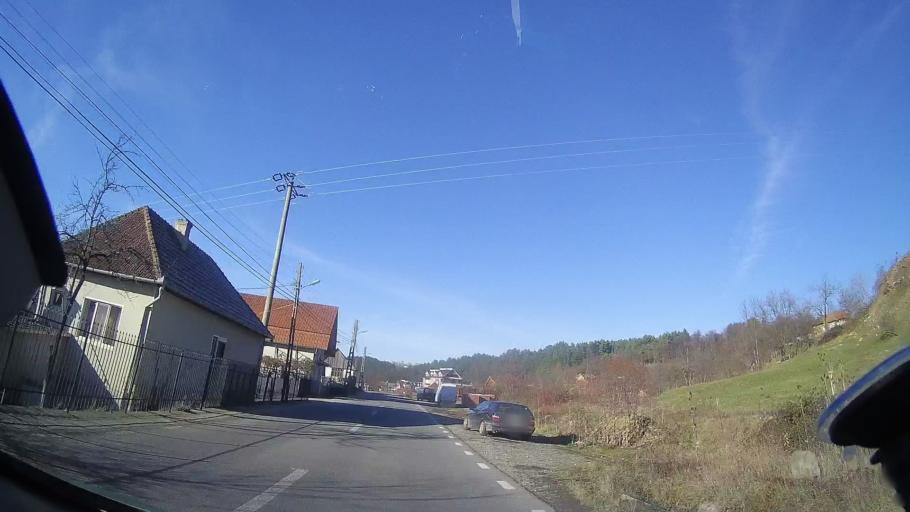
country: RO
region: Bihor
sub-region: Comuna Bratca
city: Bratca
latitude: 46.9267
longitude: 22.6087
